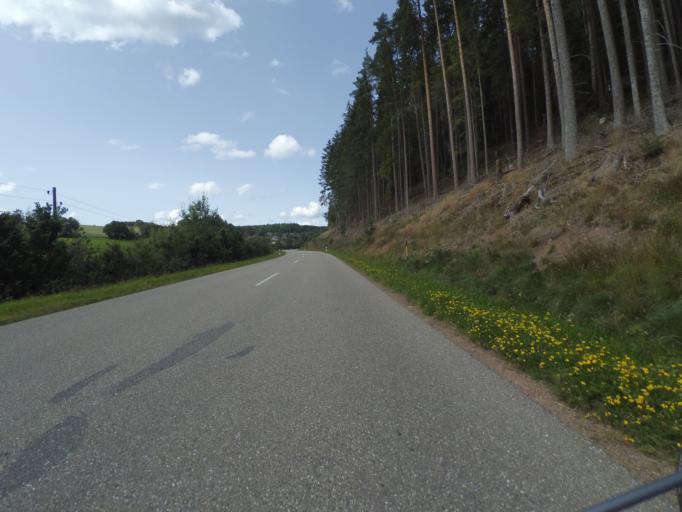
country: DE
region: Baden-Wuerttemberg
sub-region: Freiburg Region
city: Friedenweiler
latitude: 47.9107
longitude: 8.2629
